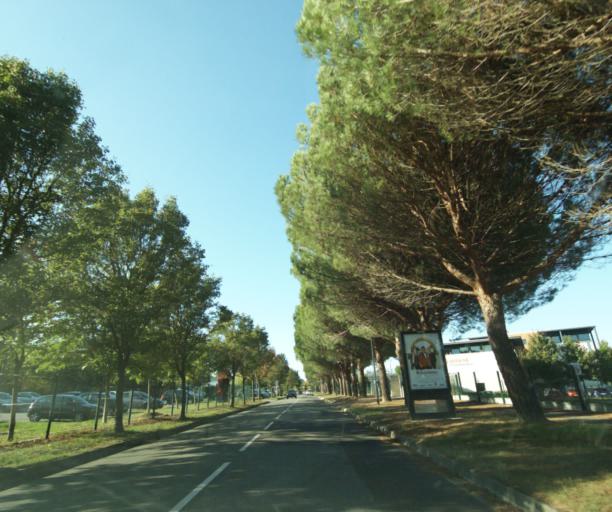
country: FR
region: Midi-Pyrenees
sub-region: Departement de la Haute-Garonne
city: Balma
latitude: 43.5796
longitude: 1.4957
